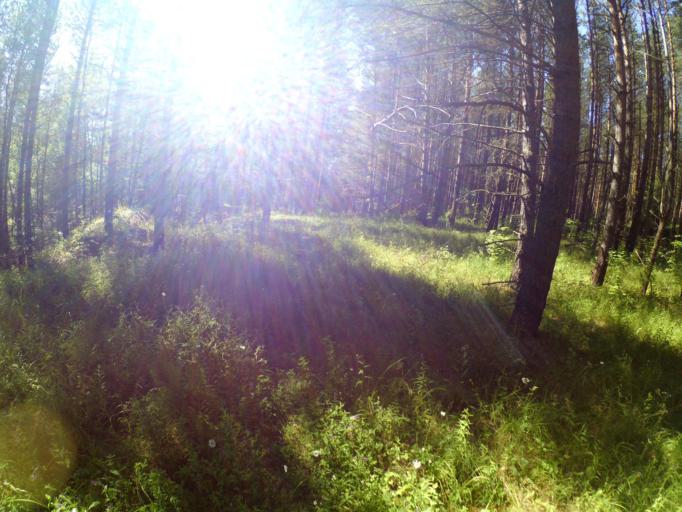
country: RU
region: Moskovskaya
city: Fosforitnyy
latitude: 55.3373
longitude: 38.9258
